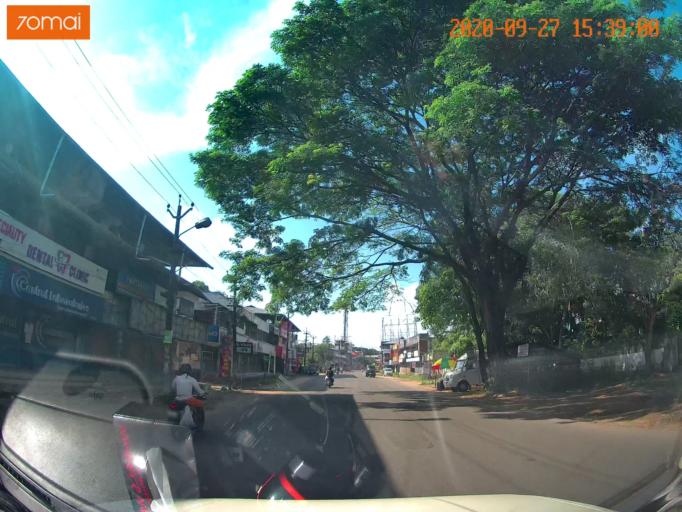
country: IN
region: Kerala
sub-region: Thrissur District
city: Thanniyam
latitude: 10.4664
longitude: 76.0821
